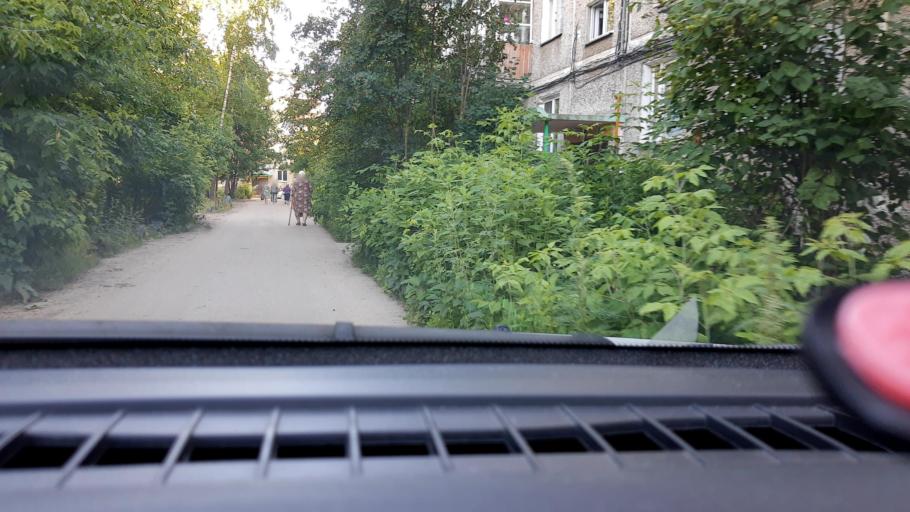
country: RU
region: Nizjnij Novgorod
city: Dzerzhinsk
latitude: 56.2275
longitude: 43.4228
